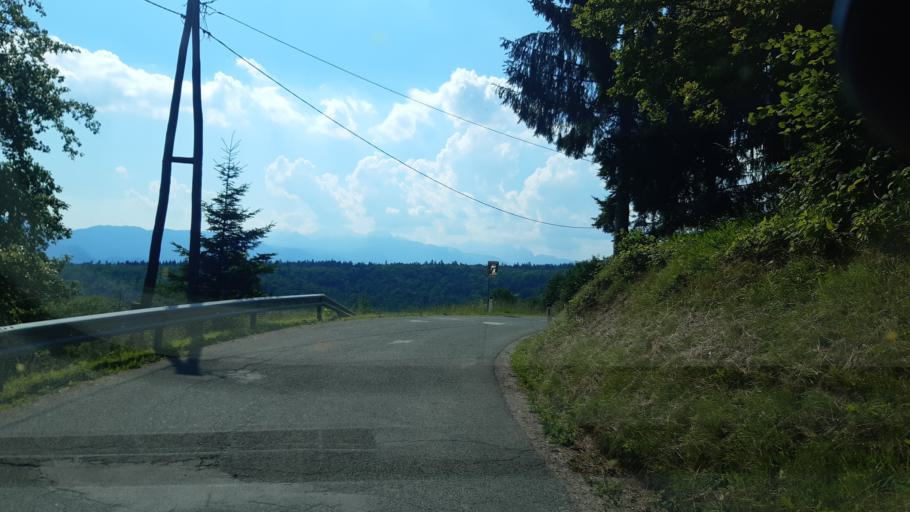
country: SI
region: Radovljica
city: Radovljica
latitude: 46.3666
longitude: 14.2306
